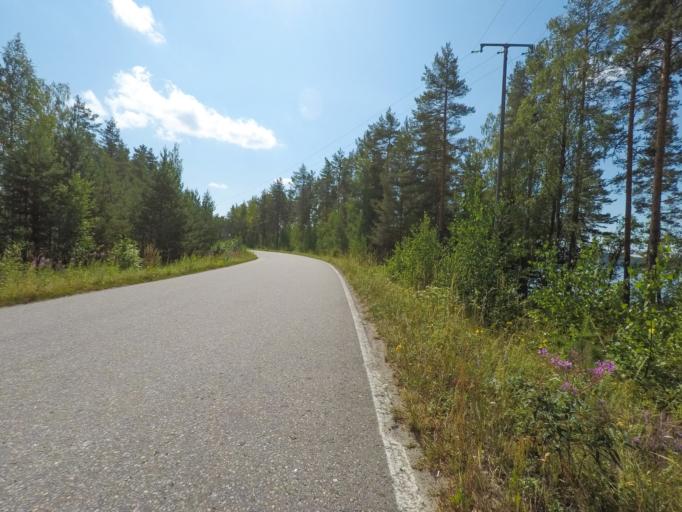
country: FI
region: Southern Savonia
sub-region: Mikkeli
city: Puumala
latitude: 61.5031
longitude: 28.1670
